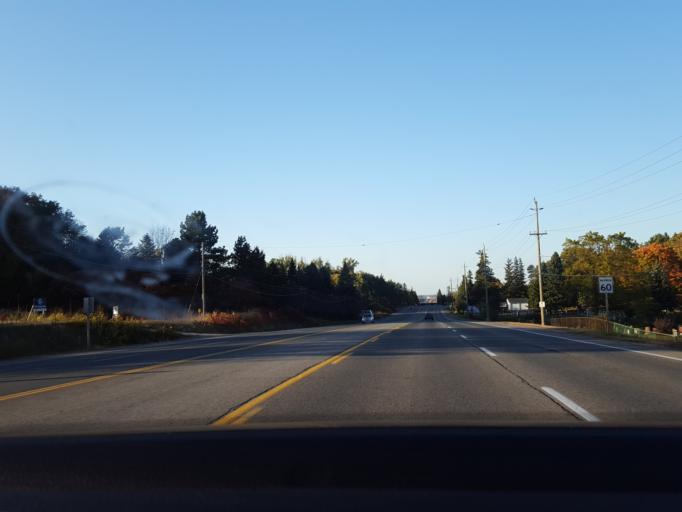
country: CA
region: Ontario
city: Newmarket
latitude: 43.9740
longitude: -79.4614
